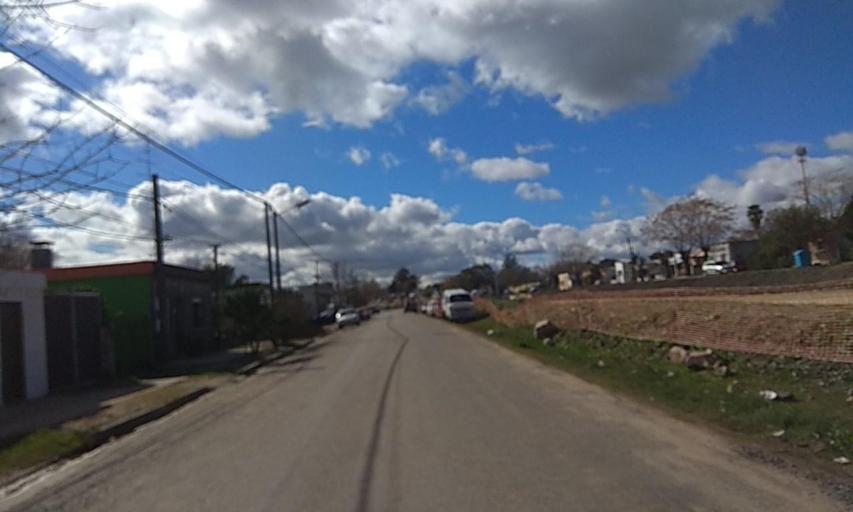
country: UY
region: Florida
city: Florida
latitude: -34.0892
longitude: -56.2197
